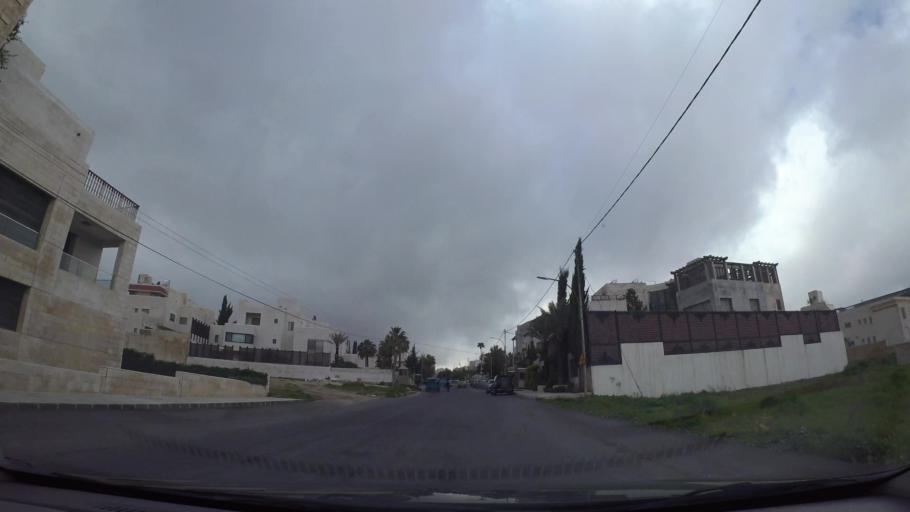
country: JO
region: Amman
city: Amman
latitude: 31.9488
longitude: 35.8986
